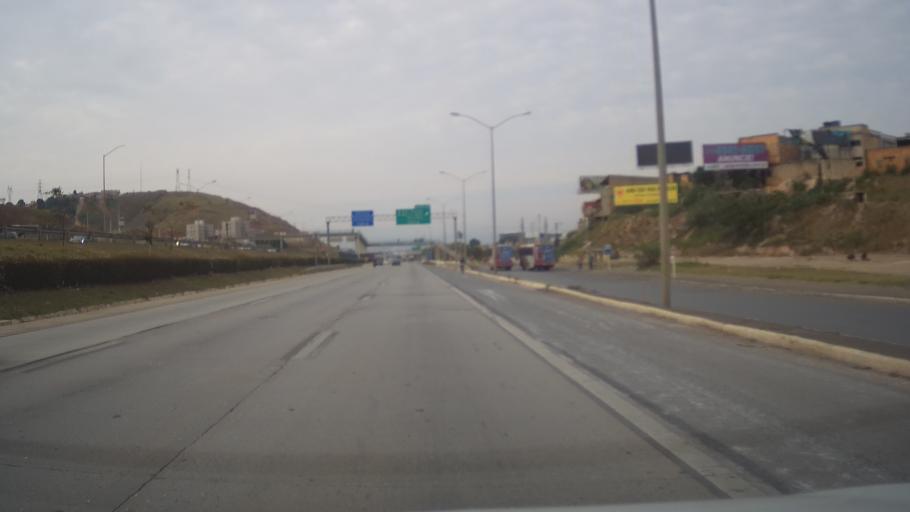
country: BR
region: Minas Gerais
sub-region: Vespasiano
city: Vespasiano
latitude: -19.7700
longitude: -43.9486
